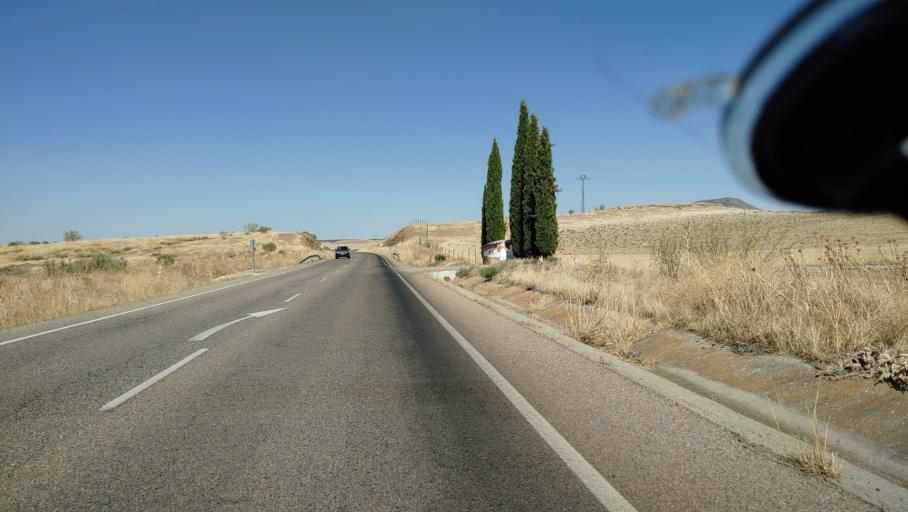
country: ES
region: Castille-La Mancha
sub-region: Province of Toledo
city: Casasbuenas
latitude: 39.7238
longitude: -4.1185
